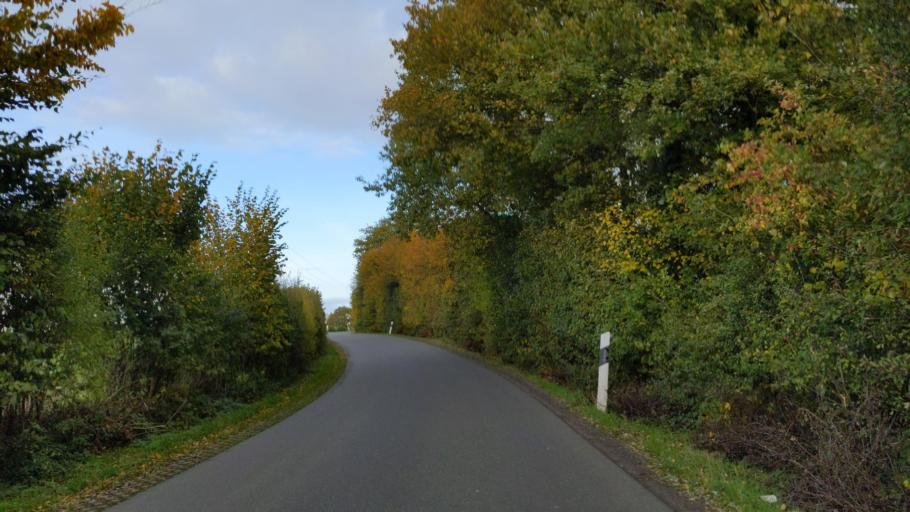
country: DE
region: Schleswig-Holstein
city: Sierksdorf
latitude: 54.1046
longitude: 10.7473
